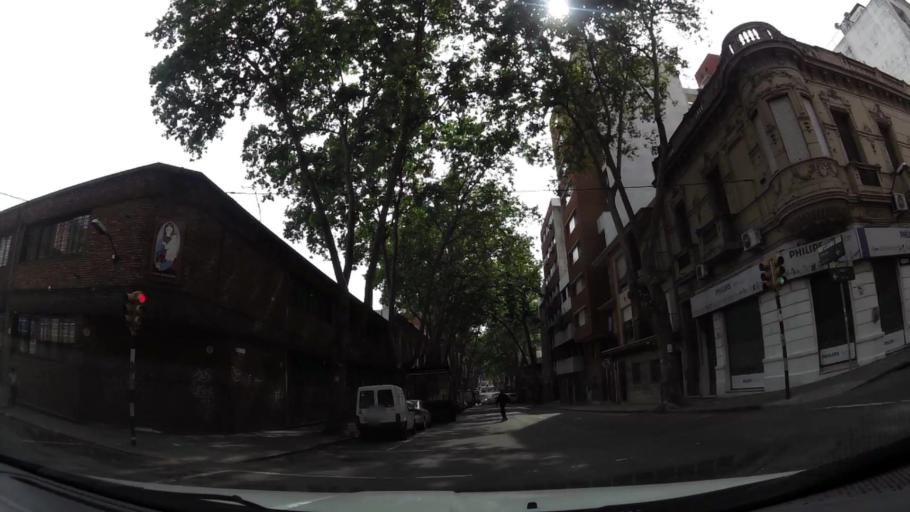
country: UY
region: Montevideo
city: Montevideo
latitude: -34.9012
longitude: -56.1796
